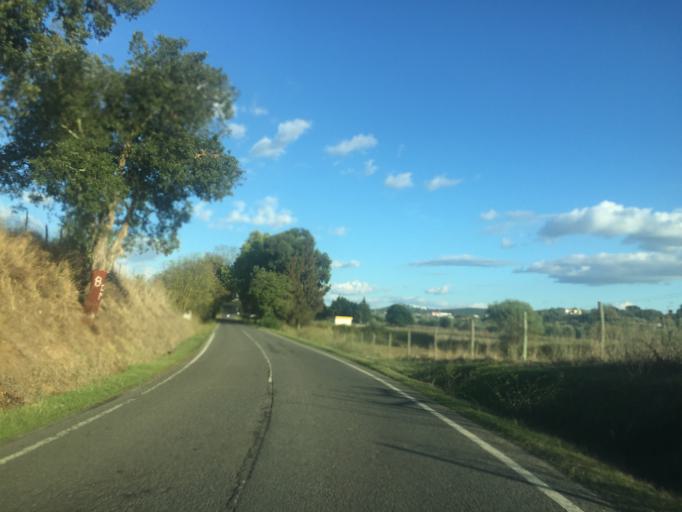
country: PT
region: Portalegre
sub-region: Alter do Chao
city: Alter do Chao
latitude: 39.1962
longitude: -7.6758
